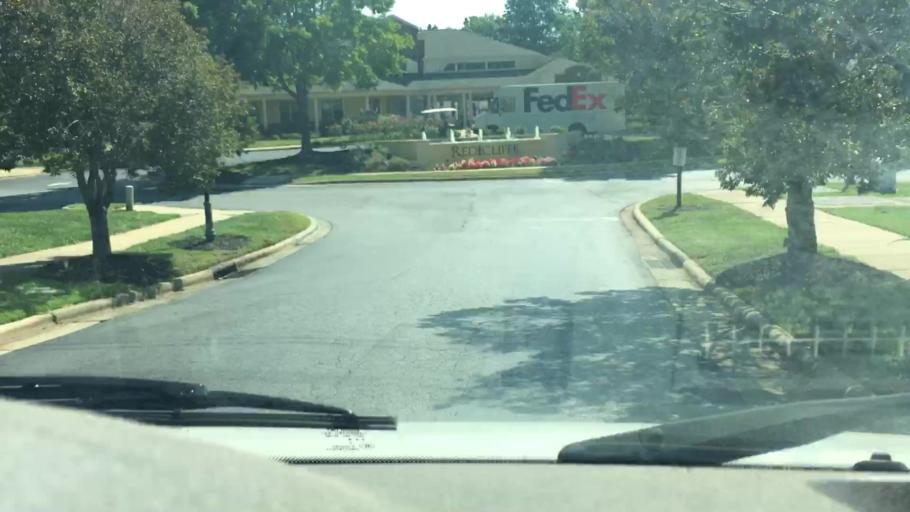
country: US
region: North Carolina
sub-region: Mecklenburg County
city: Cornelius
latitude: 35.4489
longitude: -80.8884
